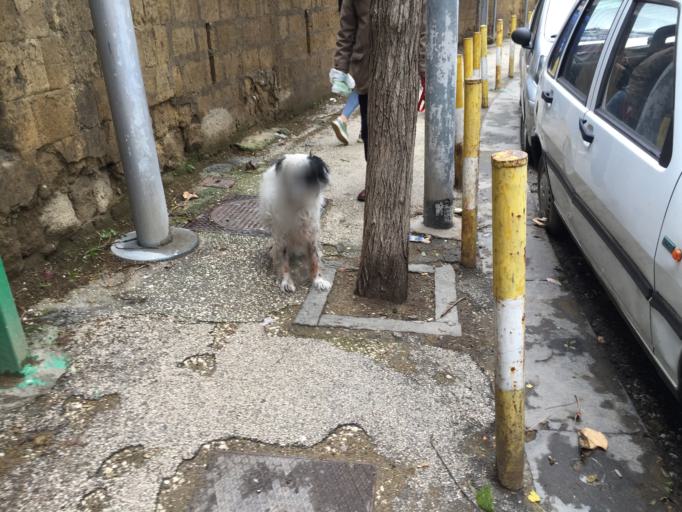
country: IT
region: Campania
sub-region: Provincia di Napoli
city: Napoli
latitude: 40.8573
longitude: 14.2303
